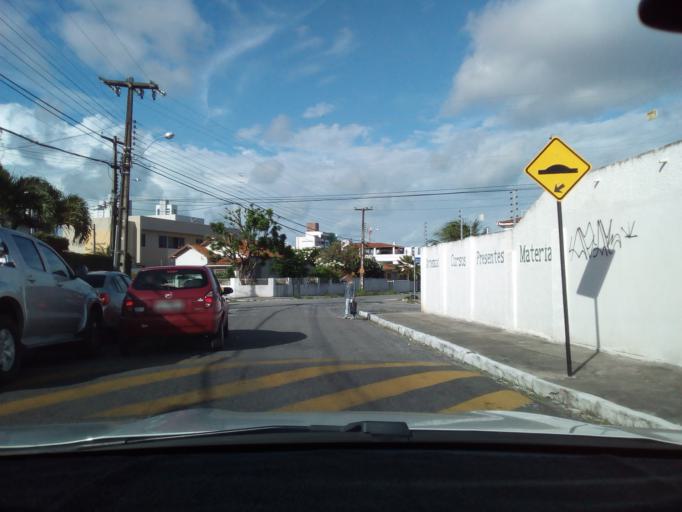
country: BR
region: Paraiba
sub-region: Joao Pessoa
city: Joao Pessoa
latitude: -7.1255
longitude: -34.8555
